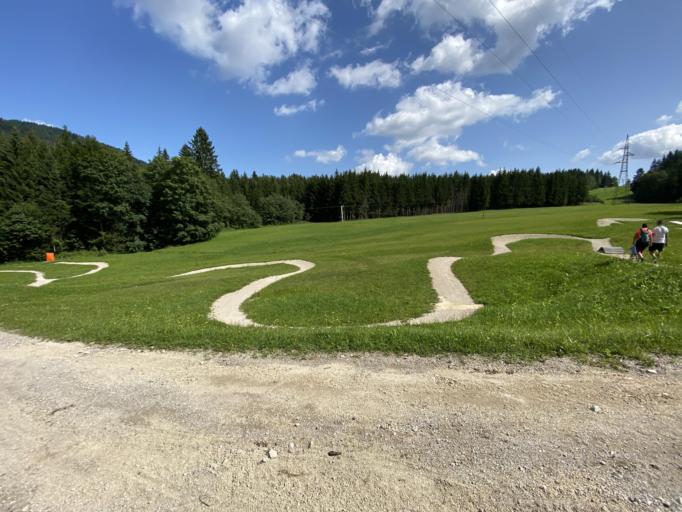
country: AT
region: Lower Austria
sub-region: Politischer Bezirk Lilienfeld
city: Annaberg
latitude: 47.8763
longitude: 15.3668
